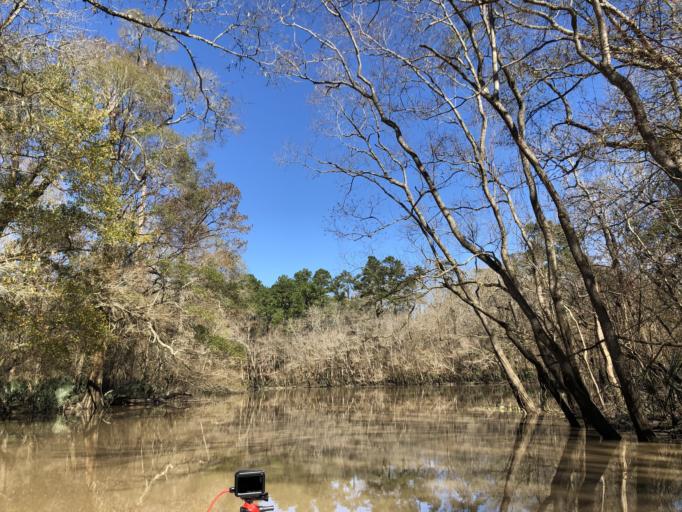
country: US
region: Louisiana
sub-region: Calcasieu Parish
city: Iowa
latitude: 30.3199
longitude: -93.0793
